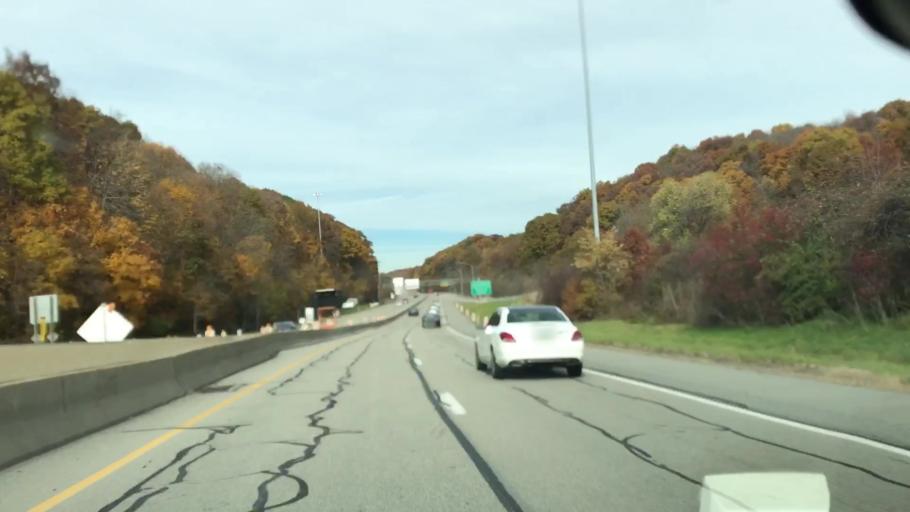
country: US
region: Pennsylvania
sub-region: Allegheny County
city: Enlow
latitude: 40.4698
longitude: -80.1988
